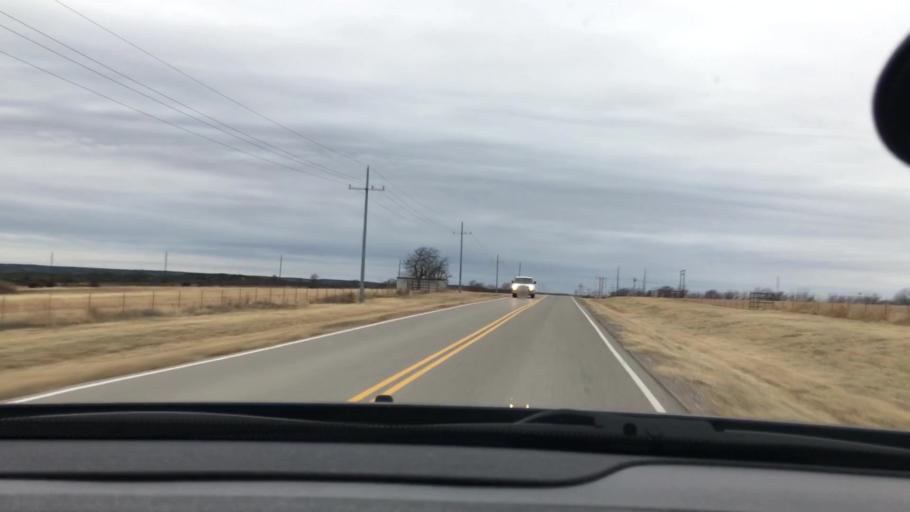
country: US
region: Oklahoma
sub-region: Murray County
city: Davis
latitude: 34.4772
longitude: -97.0963
